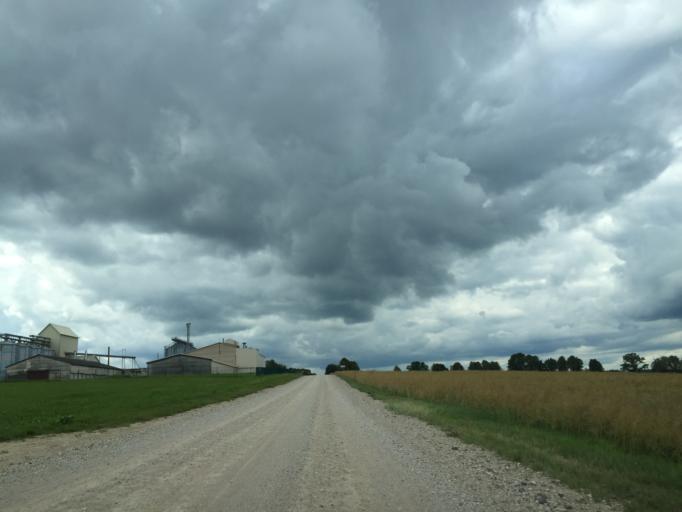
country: LV
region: Malpils
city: Malpils
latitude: 56.8567
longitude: 25.0337
